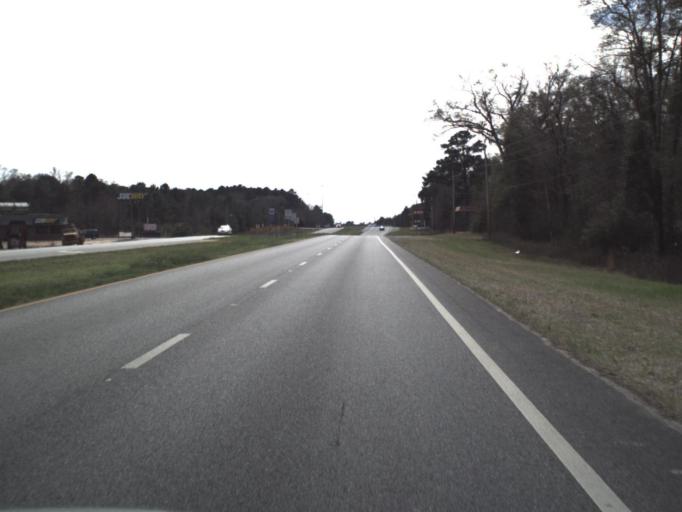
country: US
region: Florida
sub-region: Jackson County
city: Marianna
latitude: 30.7626
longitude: -85.3775
